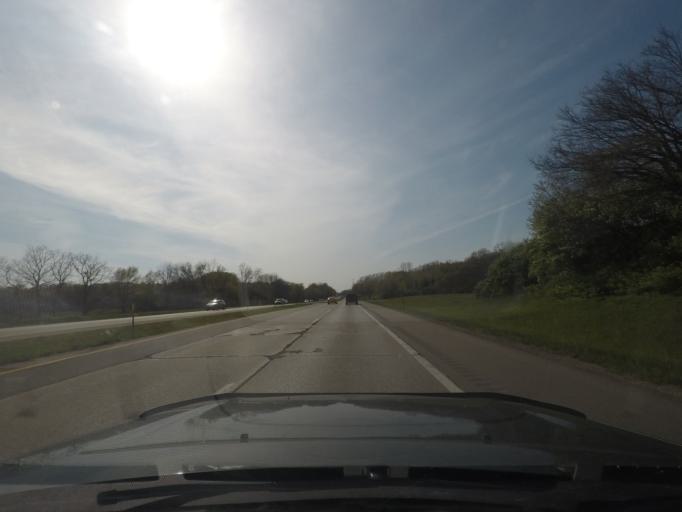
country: US
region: Michigan
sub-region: Berrien County
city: Niles
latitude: 41.8020
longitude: -86.2824
